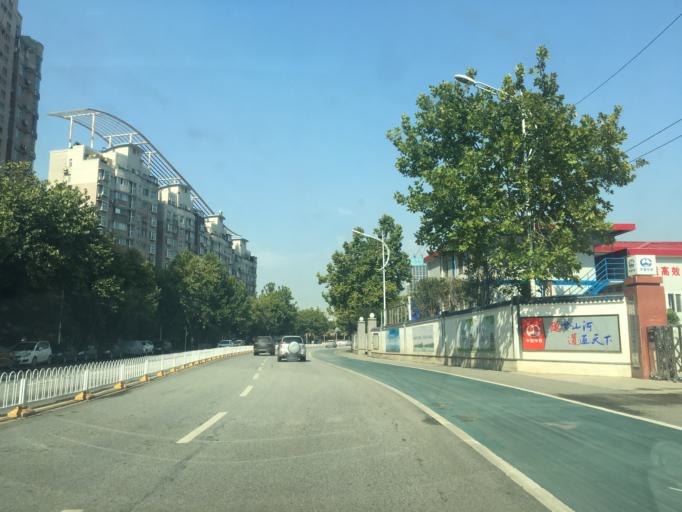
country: CN
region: Hubei
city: Jiang'an
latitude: 30.5717
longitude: 114.3072
